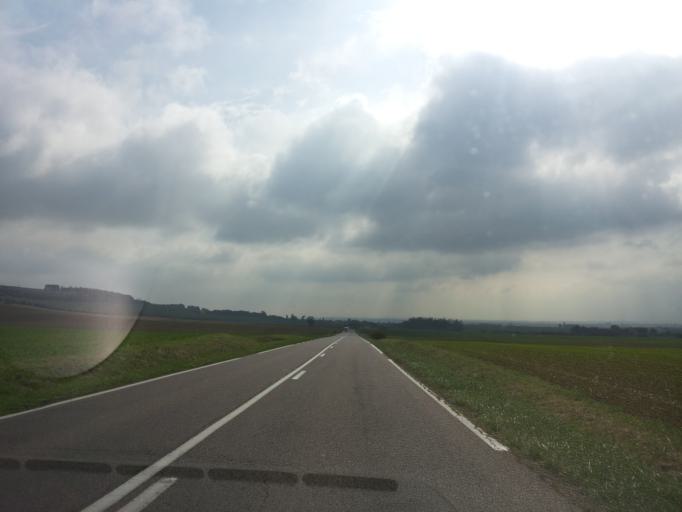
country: FR
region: Lorraine
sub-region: Departement de la Moselle
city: Solgne
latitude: 48.9292
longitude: 6.3289
